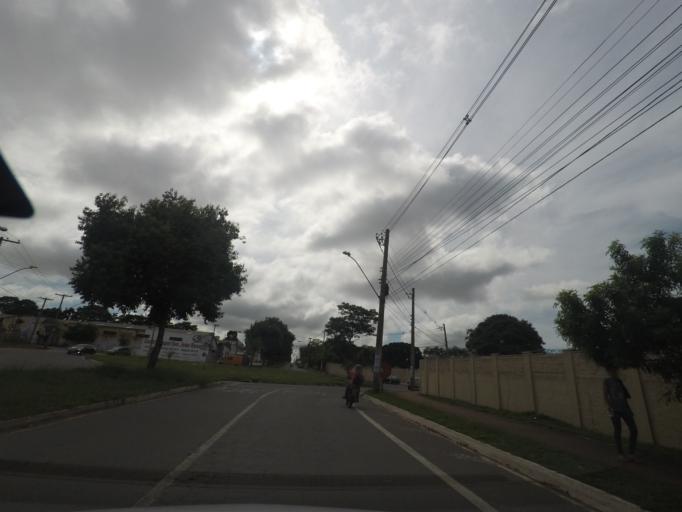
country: BR
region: Goias
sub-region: Goiania
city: Goiania
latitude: -16.6575
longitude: -49.2028
